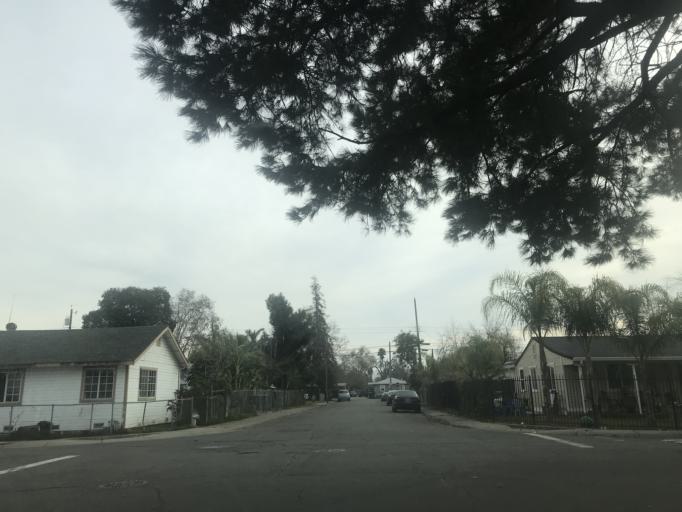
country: US
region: California
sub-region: Sacramento County
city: Parkway
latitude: 38.5301
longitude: -121.4682
